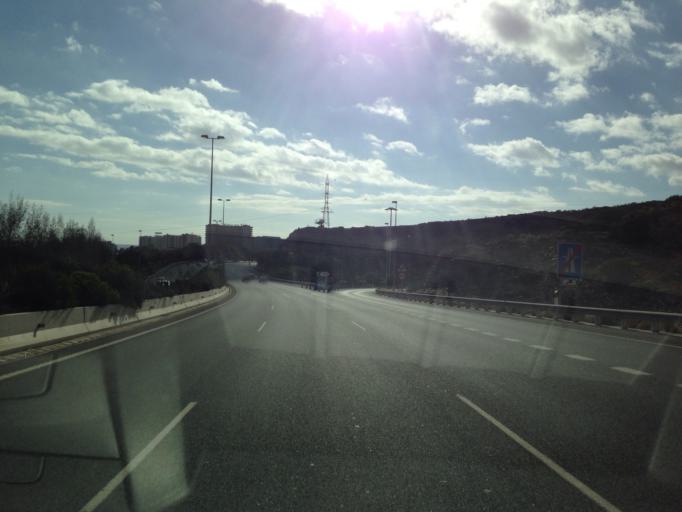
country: ES
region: Canary Islands
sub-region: Provincia de Las Palmas
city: Playa del Ingles
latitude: 27.7728
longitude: -15.5551
